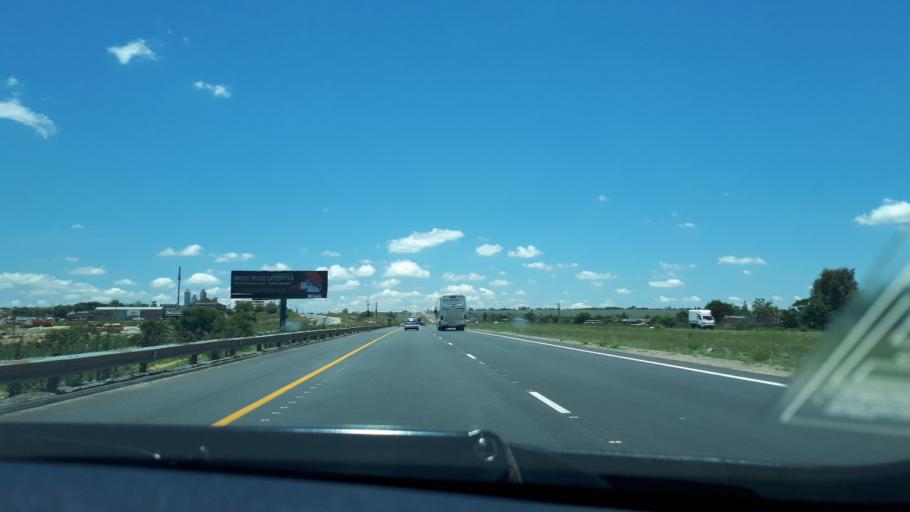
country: ZA
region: Gauteng
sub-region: City of Johannesburg Metropolitan Municipality
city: Diepsloot
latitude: -25.9262
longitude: 28.0026
